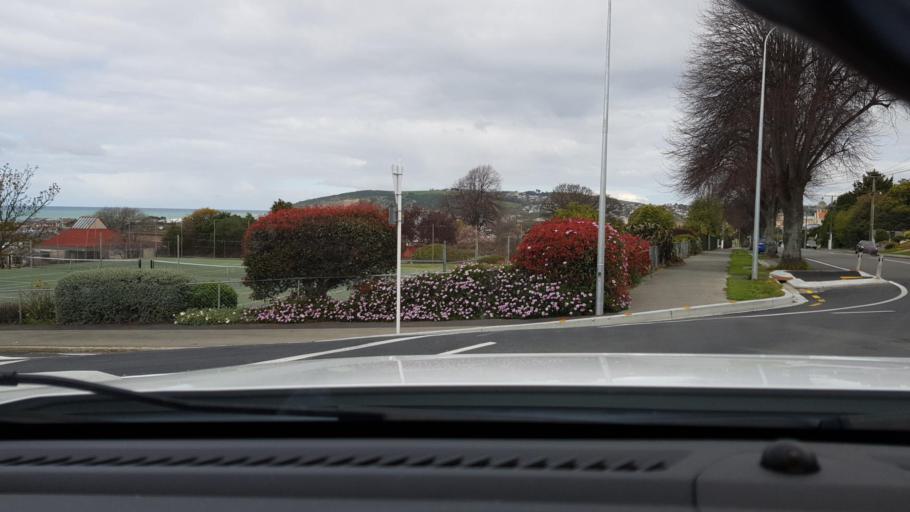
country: NZ
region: Otago
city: Oamaru
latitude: -45.0875
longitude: 170.9728
